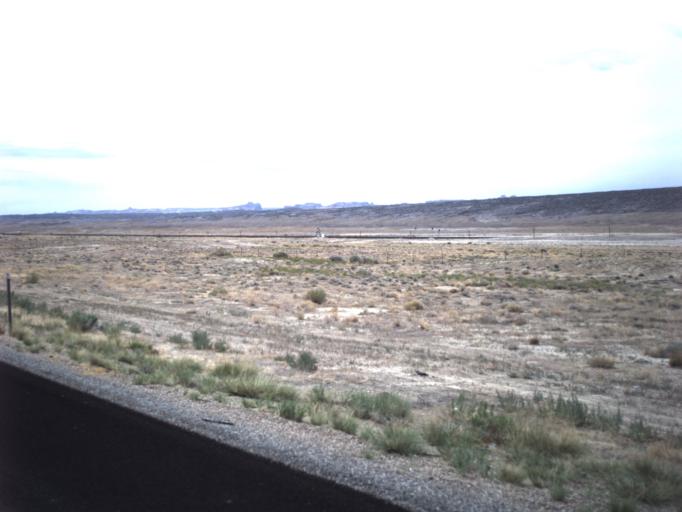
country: US
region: Utah
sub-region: Carbon County
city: East Carbon City
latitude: 39.1764
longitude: -110.3384
